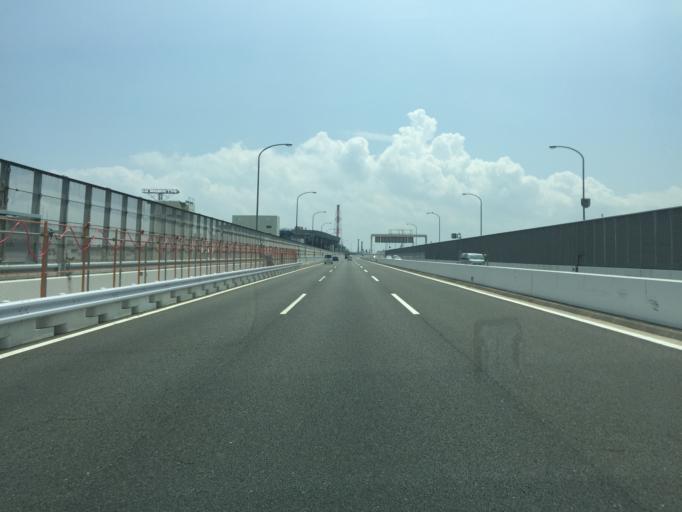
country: JP
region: Kanagawa
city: Yokohama
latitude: 35.4222
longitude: 139.6708
